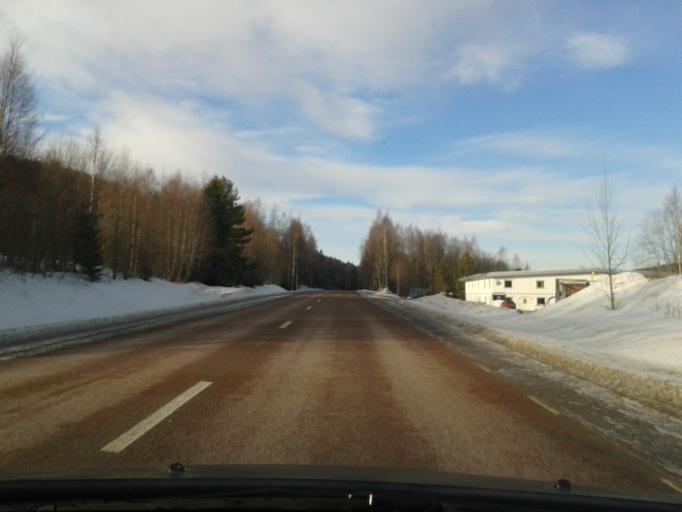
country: SE
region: Vaesternorrland
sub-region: OErnskoeldsviks Kommun
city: Bjasta
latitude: 63.3399
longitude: 18.5081
